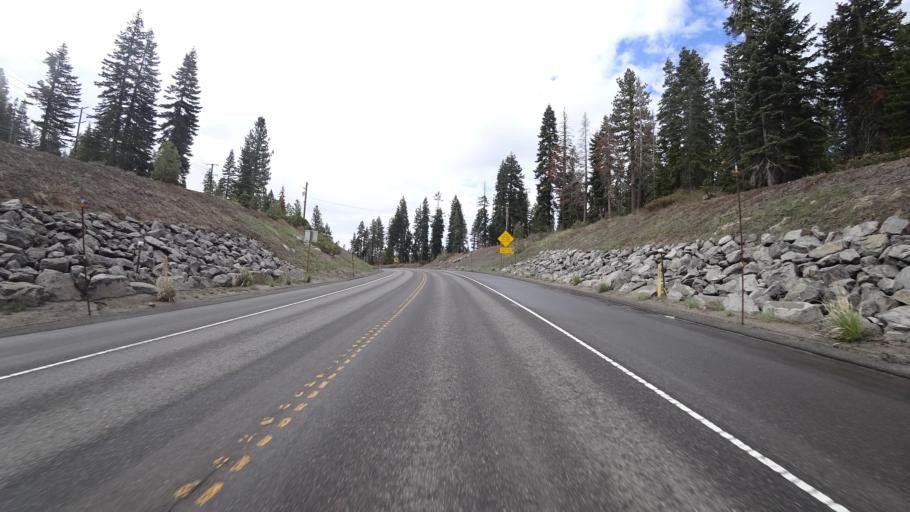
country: US
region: California
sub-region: Placer County
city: Tahoe Vista
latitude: 39.2620
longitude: -120.0719
